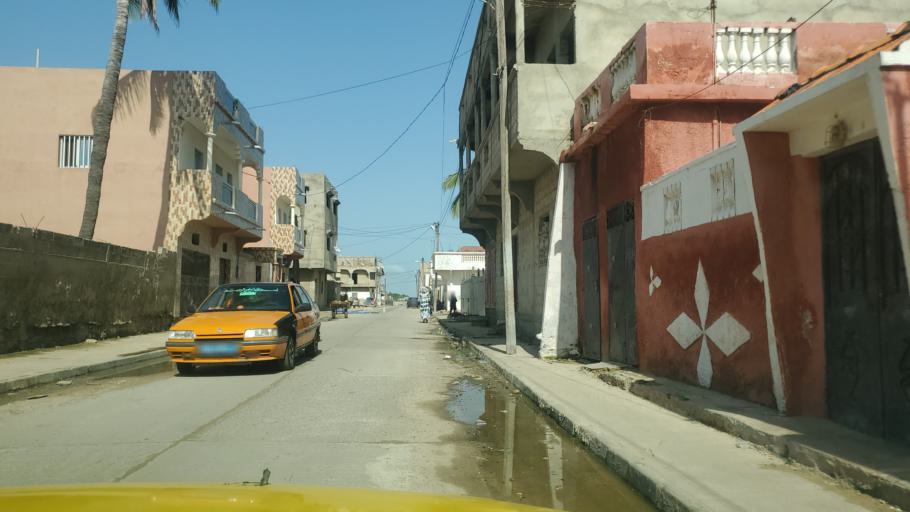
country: SN
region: Saint-Louis
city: Saint-Louis
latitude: 16.0217
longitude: -16.4850
